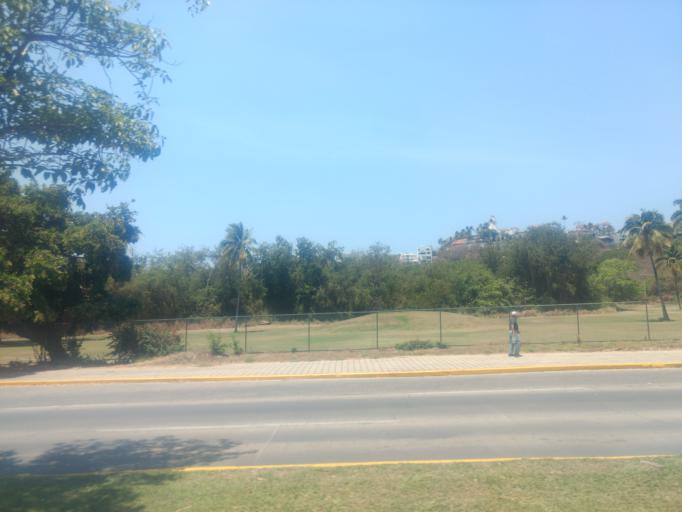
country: MX
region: Colima
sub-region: Manzanillo
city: Manzanillo
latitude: 19.1143
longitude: -104.3449
